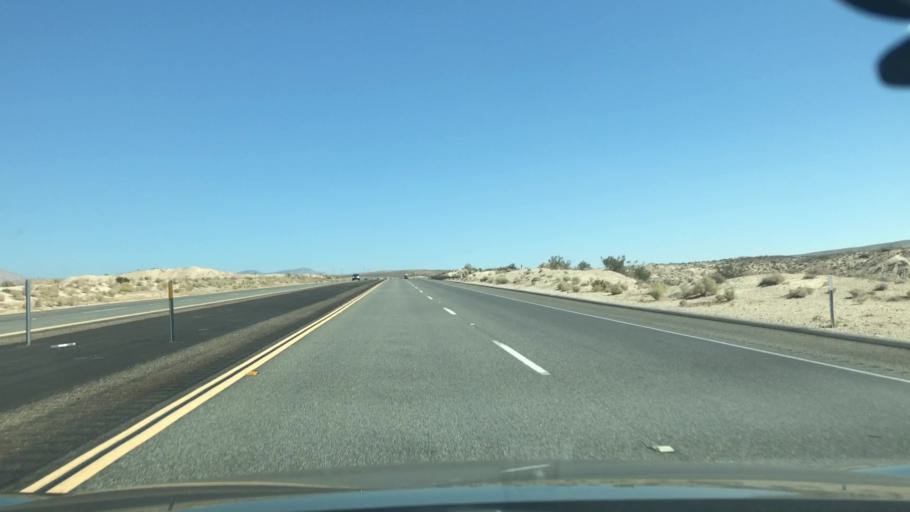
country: US
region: California
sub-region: Kern County
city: California City
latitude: 35.3908
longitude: -117.9850
